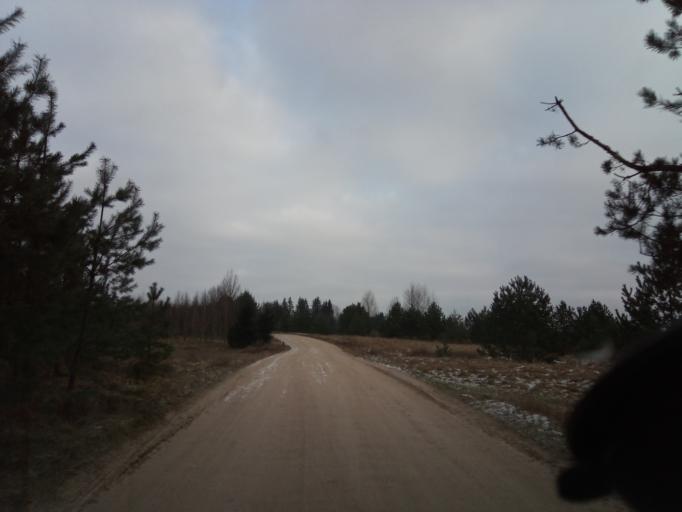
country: LT
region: Alytaus apskritis
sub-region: Alytaus rajonas
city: Daugai
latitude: 54.3617
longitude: 24.4419
